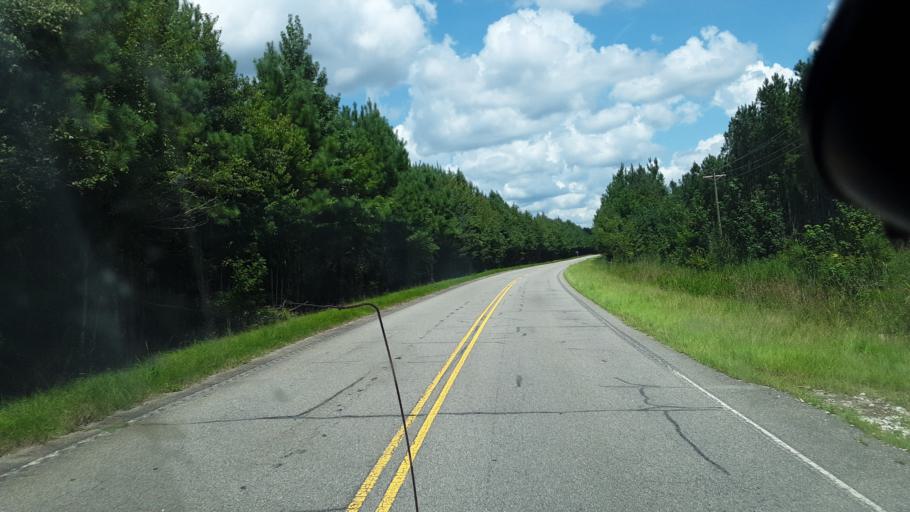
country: US
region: South Carolina
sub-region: Williamsburg County
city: Andrews
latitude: 33.5363
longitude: -79.4838
